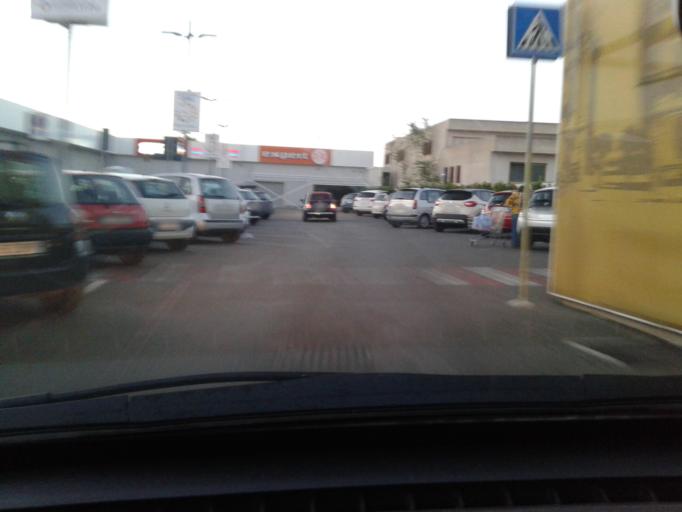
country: IT
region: Sicily
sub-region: Palermo
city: Palermo
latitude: 38.1034
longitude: 13.3256
